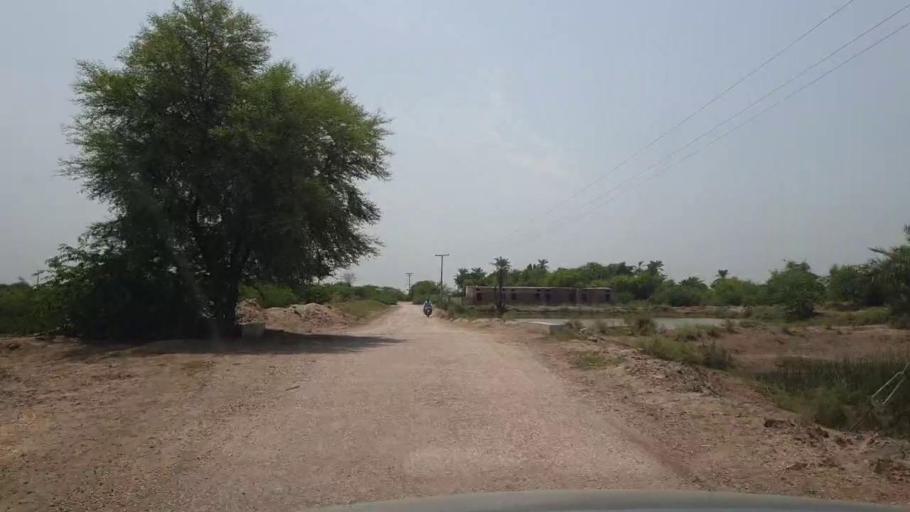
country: PK
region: Sindh
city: Garhi Yasin
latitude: 27.8789
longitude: 68.4953
